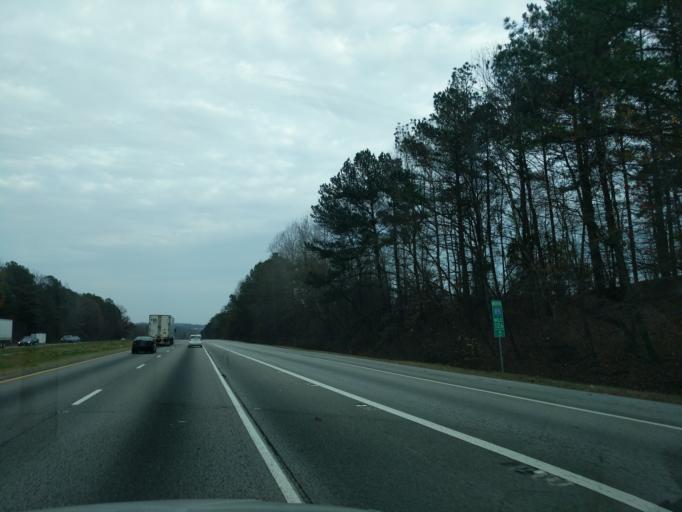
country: US
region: Georgia
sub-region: Jackson County
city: Hoschton
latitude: 34.0975
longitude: -83.8088
